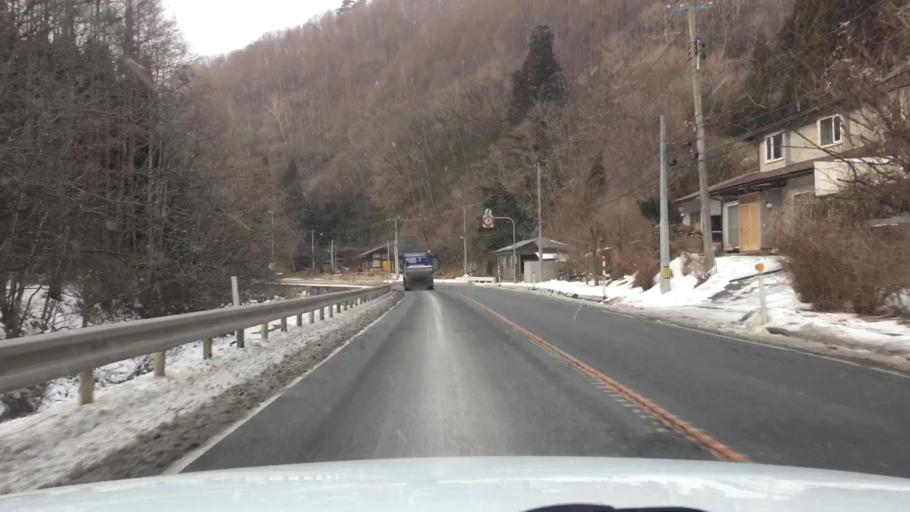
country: JP
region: Iwate
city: Tono
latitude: 39.6149
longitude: 141.4811
